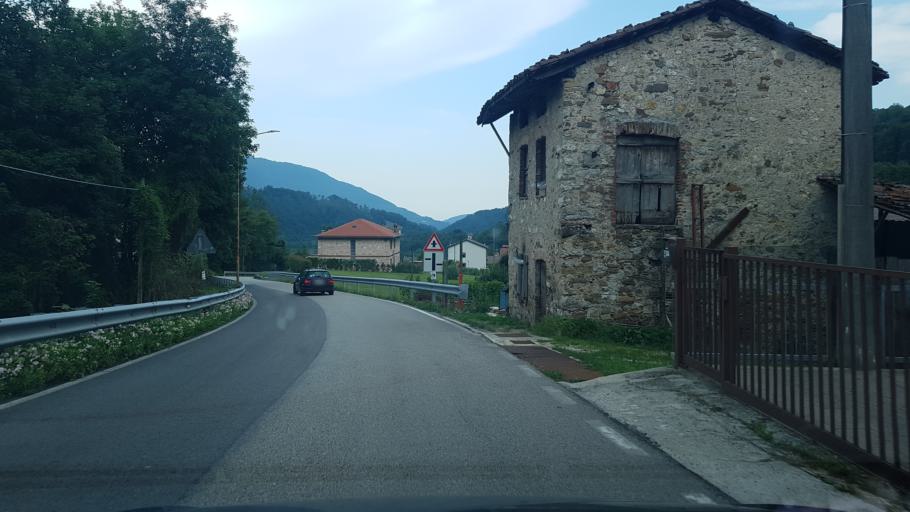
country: IT
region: Veneto
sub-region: Provincia di Vicenza
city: Valli del Pasubio
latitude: 45.7541
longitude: 11.2227
